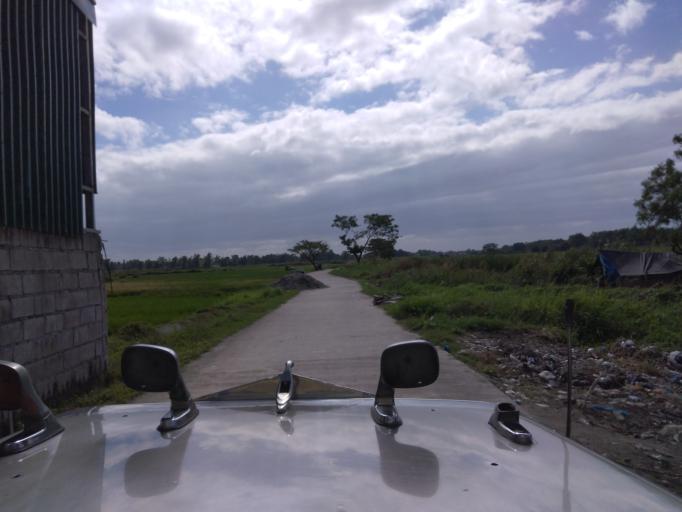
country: PH
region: Central Luzon
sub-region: Province of Pampanga
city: San Patricio
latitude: 15.0880
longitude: 120.7171
